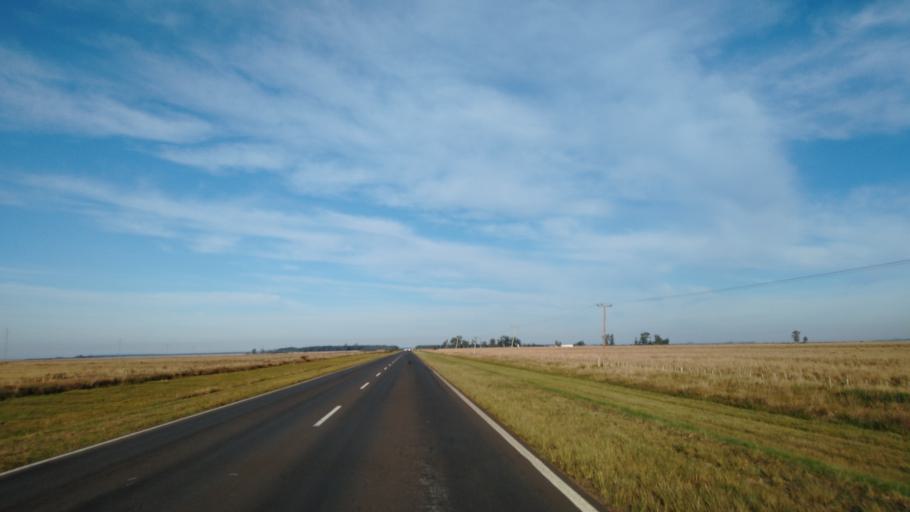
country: AR
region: Corrientes
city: La Cruz
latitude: -29.2297
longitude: -56.7199
